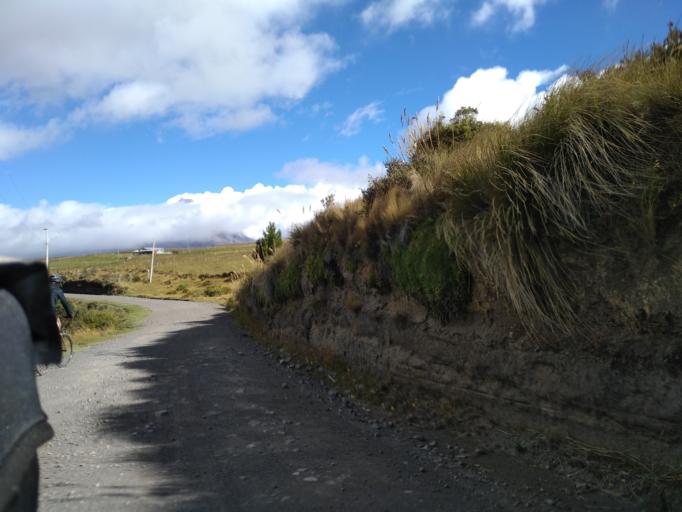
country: EC
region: Pichincha
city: Machachi
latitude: -0.5552
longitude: -78.4553
